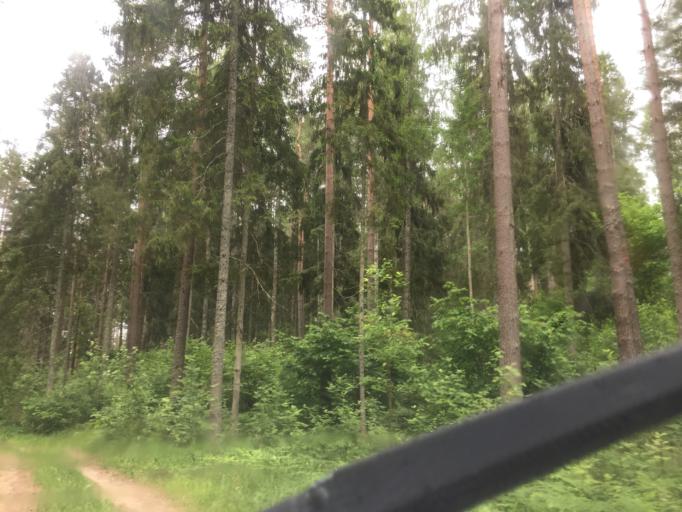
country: LV
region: Tukuma Rajons
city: Tukums
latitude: 57.0297
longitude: 23.0755
